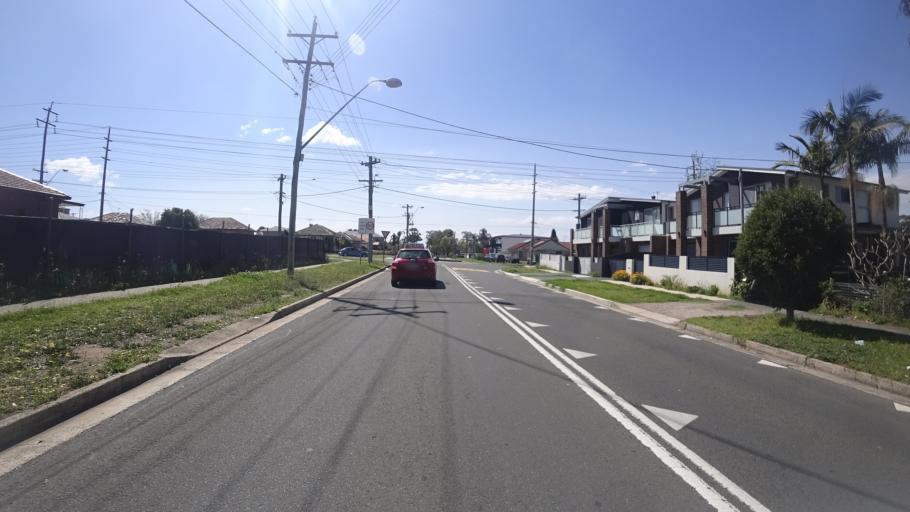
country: AU
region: New South Wales
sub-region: Liverpool
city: Miller
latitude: -33.9331
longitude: 150.9006
